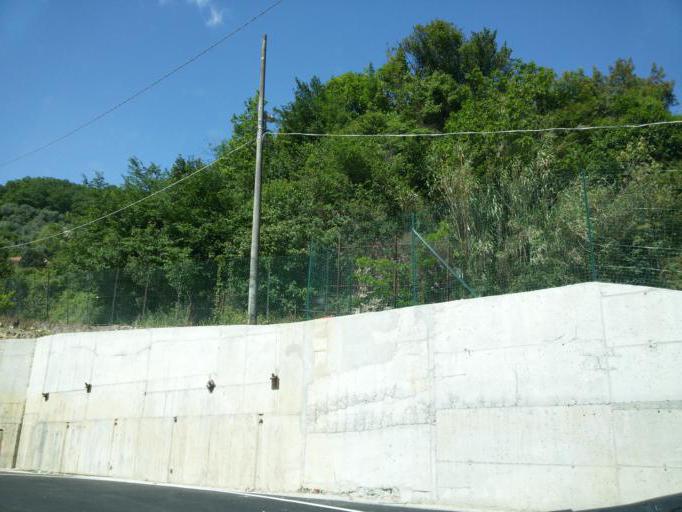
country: IT
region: Liguria
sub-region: Provincia di Genova
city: Piccarello
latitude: 44.4349
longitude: 8.9706
